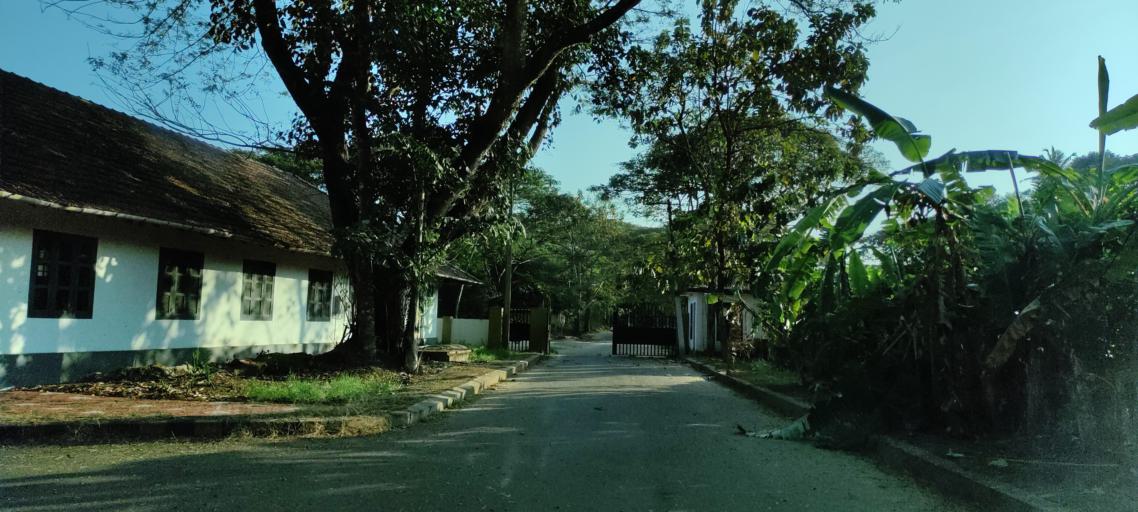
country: IN
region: Kerala
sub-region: Alappuzha
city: Vayalar
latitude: 9.6944
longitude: 76.3439
